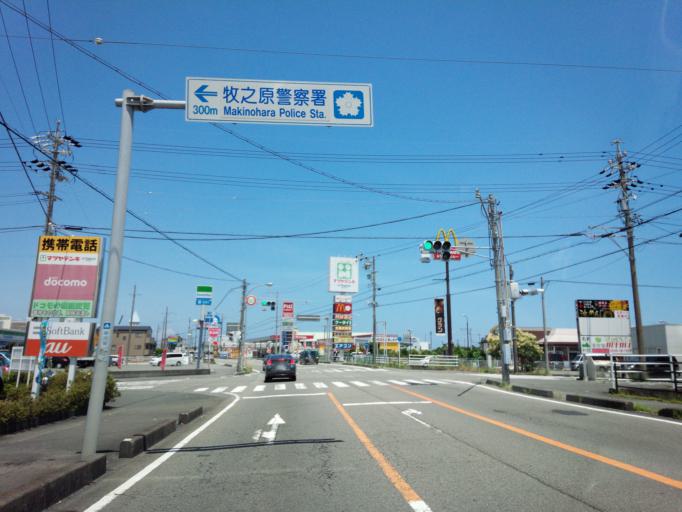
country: JP
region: Shizuoka
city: Sagara
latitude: 34.7565
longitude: 138.2428
